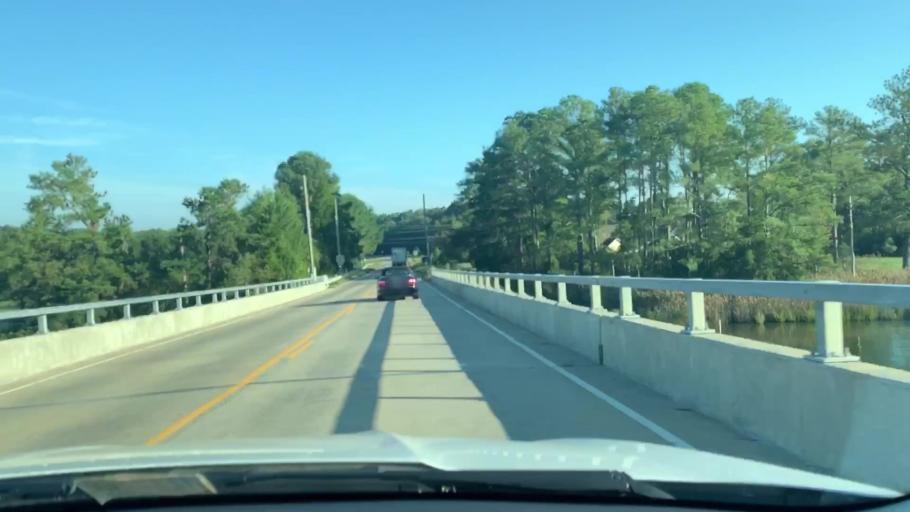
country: US
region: Virginia
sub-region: Middlesex County
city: Deltaville
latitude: 37.5126
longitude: -76.4199
